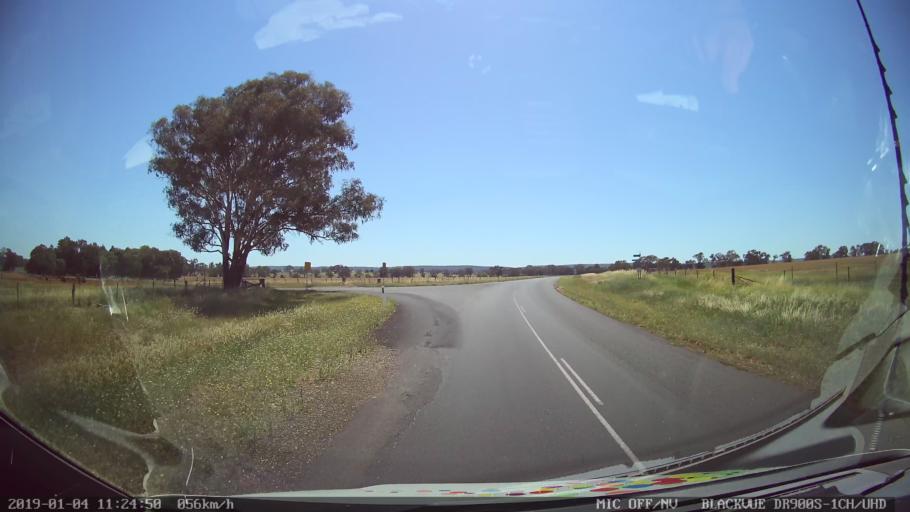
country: AU
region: New South Wales
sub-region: Cabonne
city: Molong
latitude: -33.1304
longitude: 148.7516
